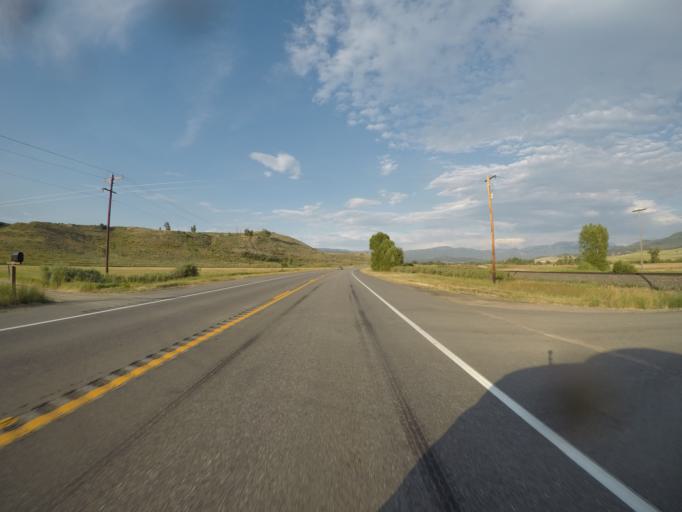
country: US
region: Colorado
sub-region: Routt County
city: Steamboat Springs
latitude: 40.4993
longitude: -106.9340
